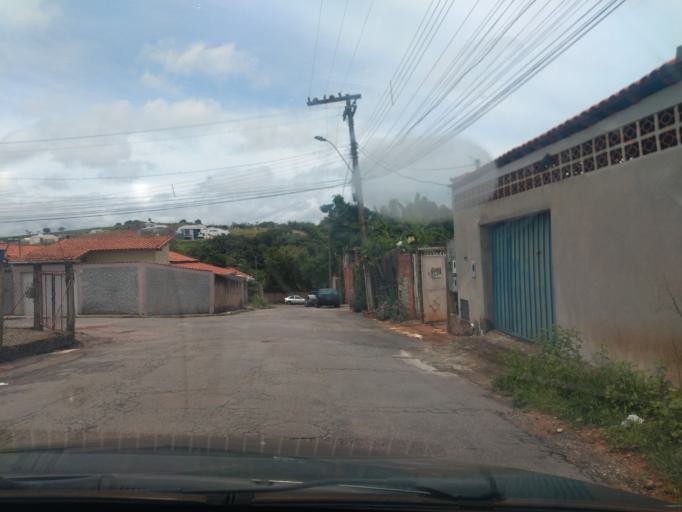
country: BR
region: Minas Gerais
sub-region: Tres Coracoes
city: Tres Coracoes
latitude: -21.6800
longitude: -45.2586
